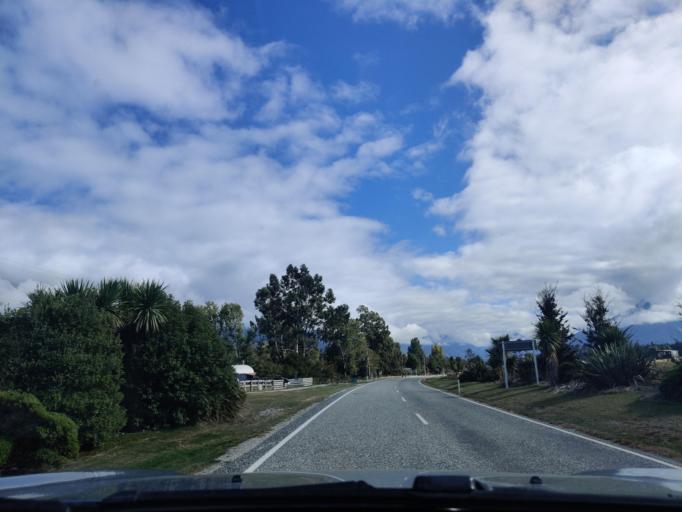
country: NZ
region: Otago
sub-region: Queenstown-Lakes District
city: Queenstown
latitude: -44.8572
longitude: 168.3920
